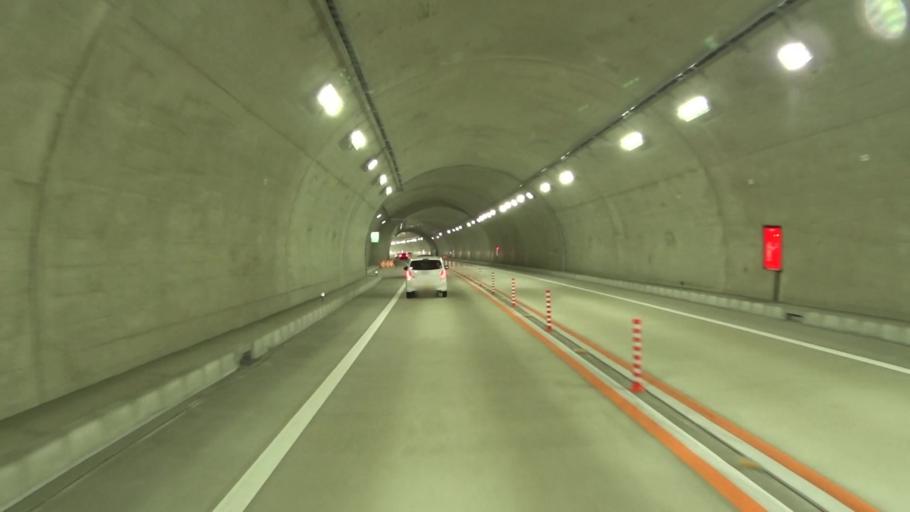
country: JP
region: Kyoto
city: Ayabe
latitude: 35.2673
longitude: 135.3454
